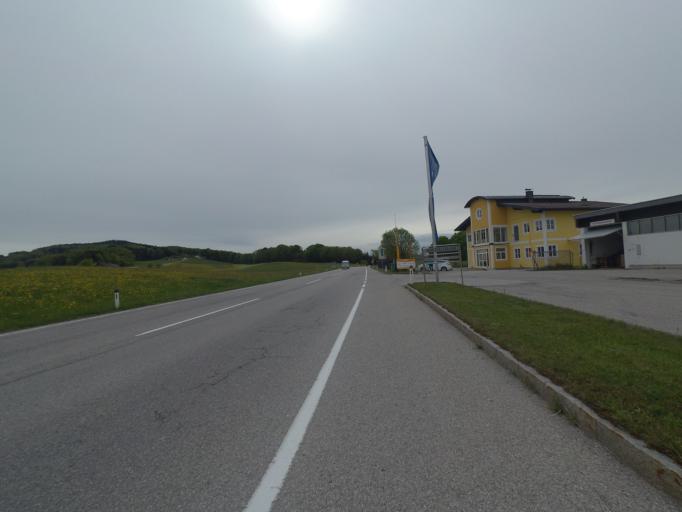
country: AT
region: Salzburg
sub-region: Politischer Bezirk Salzburg-Umgebung
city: Mattsee
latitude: 47.9704
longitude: 13.1235
